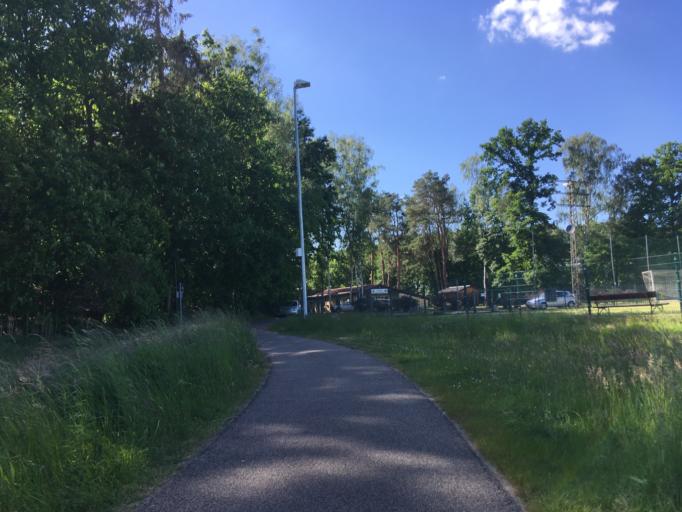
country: DE
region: Brandenburg
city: Althuttendorf
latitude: 52.9630
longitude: 13.7970
